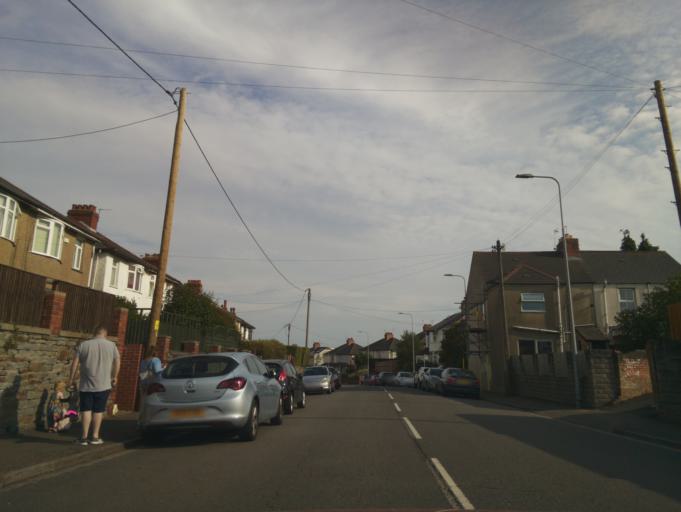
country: GB
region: Wales
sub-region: Cardiff
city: Cardiff
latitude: 51.5065
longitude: -3.1302
